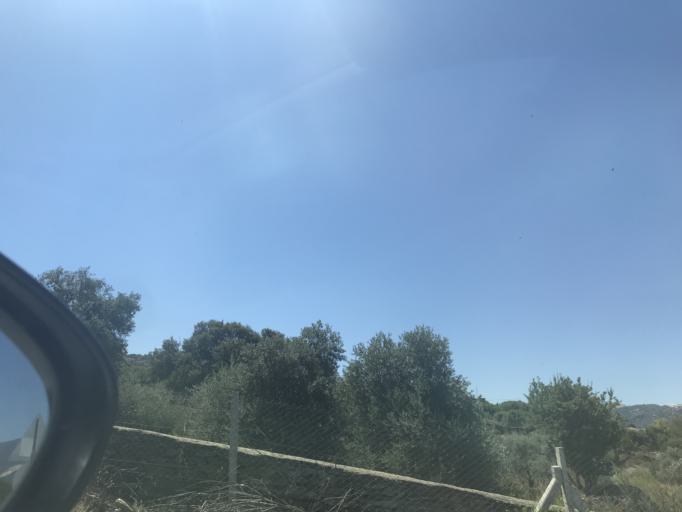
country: TR
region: Aydin
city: Akcaova
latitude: 37.4922
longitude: 28.1200
